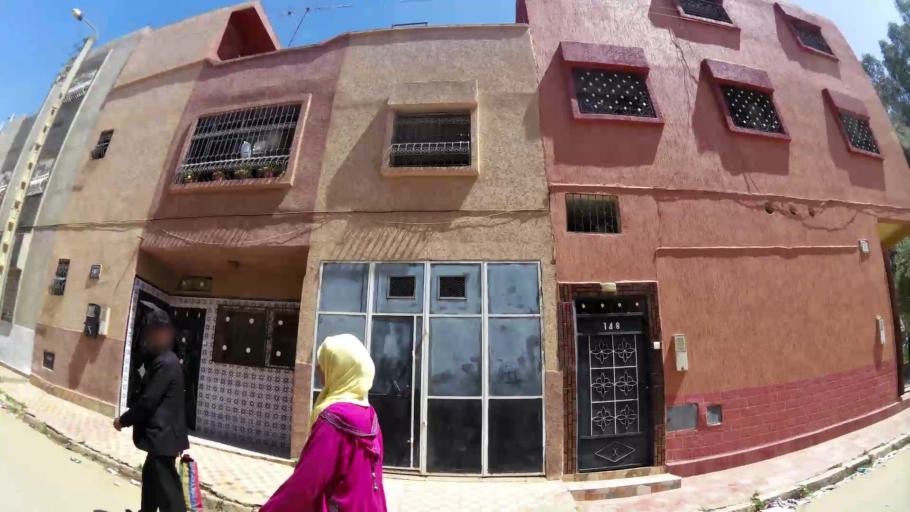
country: MA
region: Rabat-Sale-Zemmour-Zaer
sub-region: Khemisset
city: Khemisset
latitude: 33.8102
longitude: -6.0698
